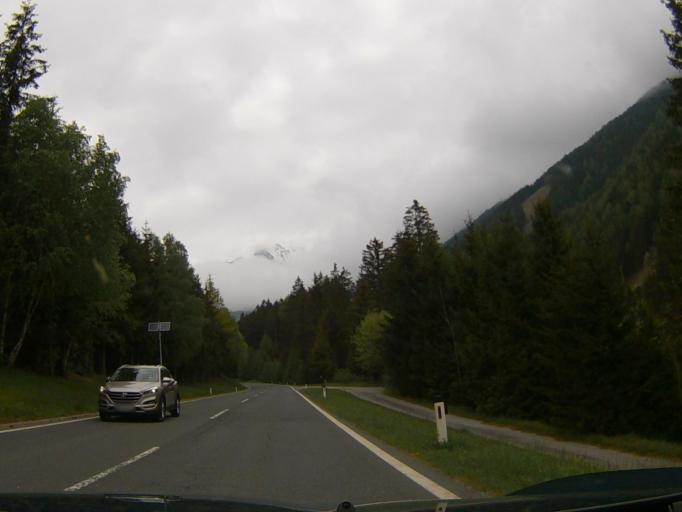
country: AT
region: Carinthia
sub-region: Politischer Bezirk Spittal an der Drau
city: Obervellach
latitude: 46.9493
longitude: 13.1820
